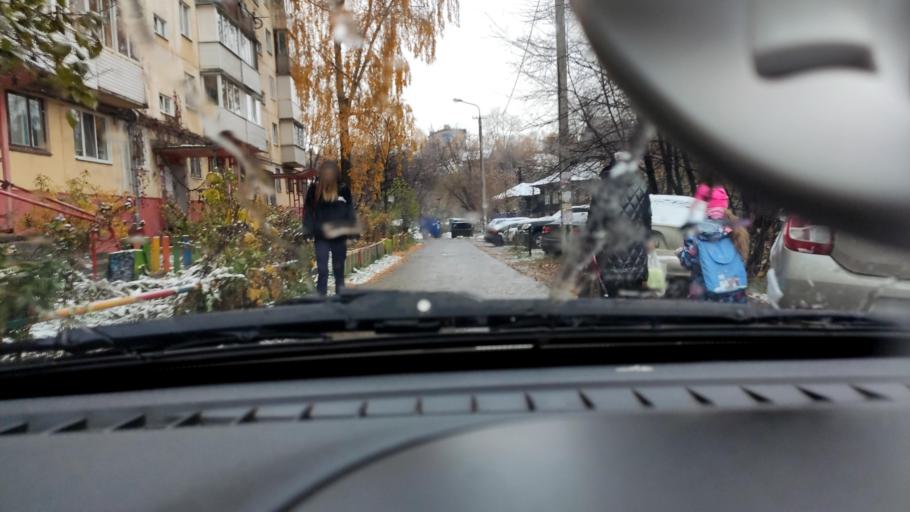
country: RU
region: Perm
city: Perm
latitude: 57.9996
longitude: 56.2160
